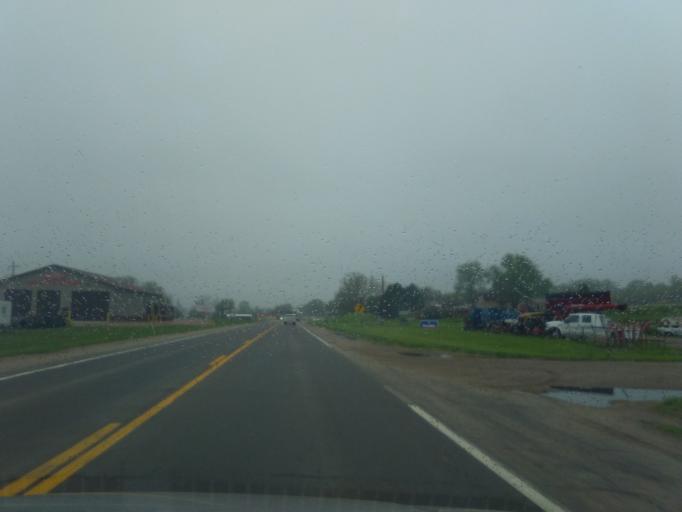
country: US
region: Nebraska
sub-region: Cuming County
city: Wisner
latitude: 41.9810
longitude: -96.9050
